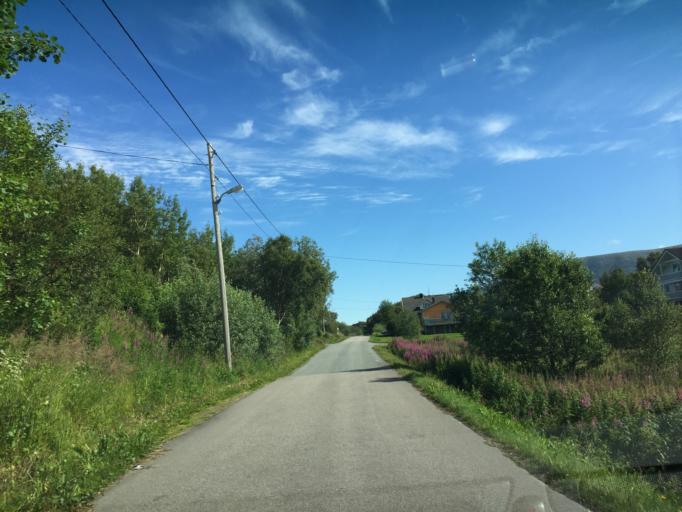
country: NO
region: Nordland
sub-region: Vagan
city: Kabelvag
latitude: 68.3901
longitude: 14.4251
